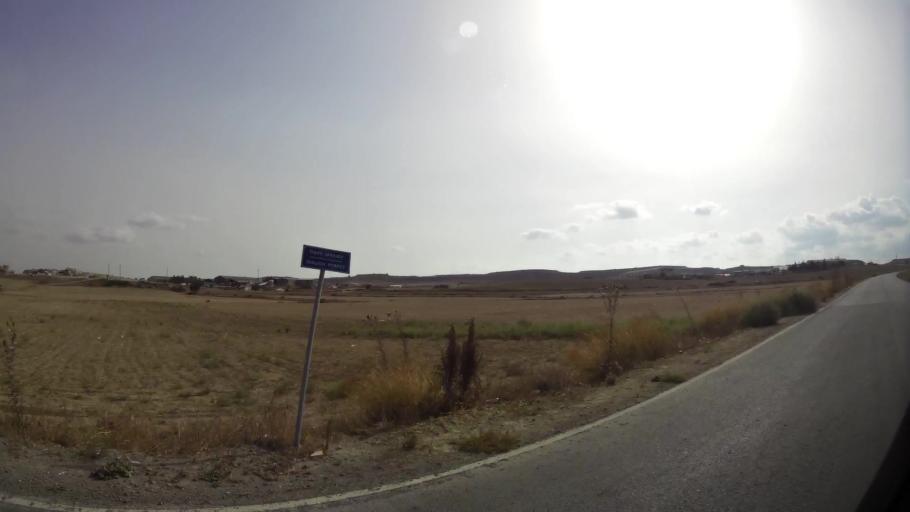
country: CY
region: Lefkosia
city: Geri
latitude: 35.0770
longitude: 33.3992
